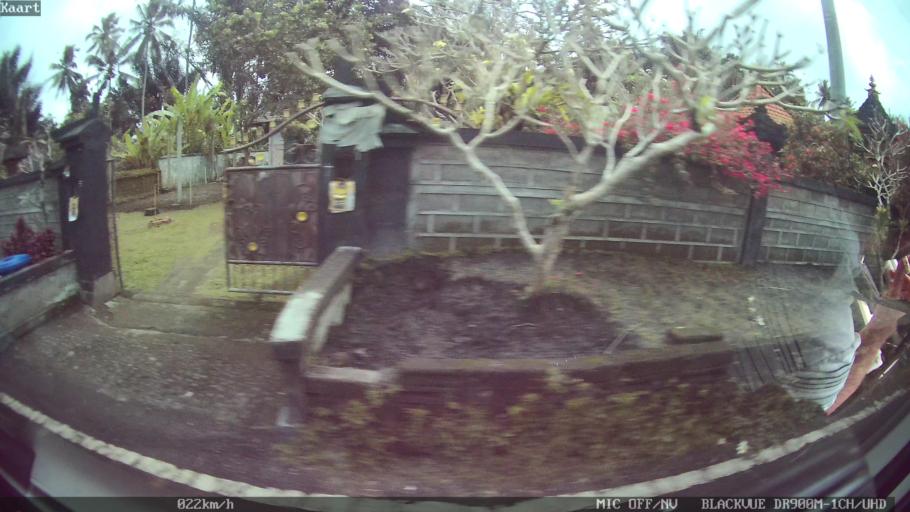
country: ID
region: Bali
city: Pemijian
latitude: -8.4544
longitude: 115.2302
